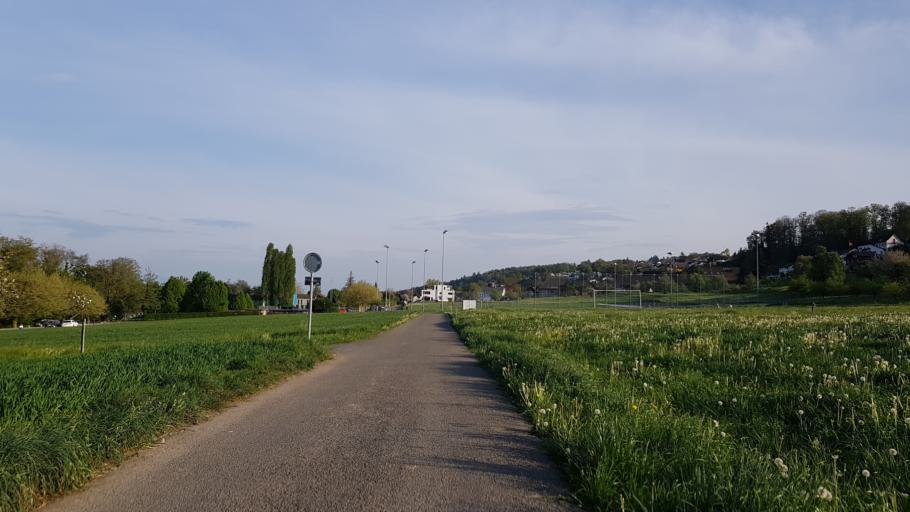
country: CH
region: Aargau
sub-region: Bezirk Kulm
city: Reinach
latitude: 47.2724
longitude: 8.2075
